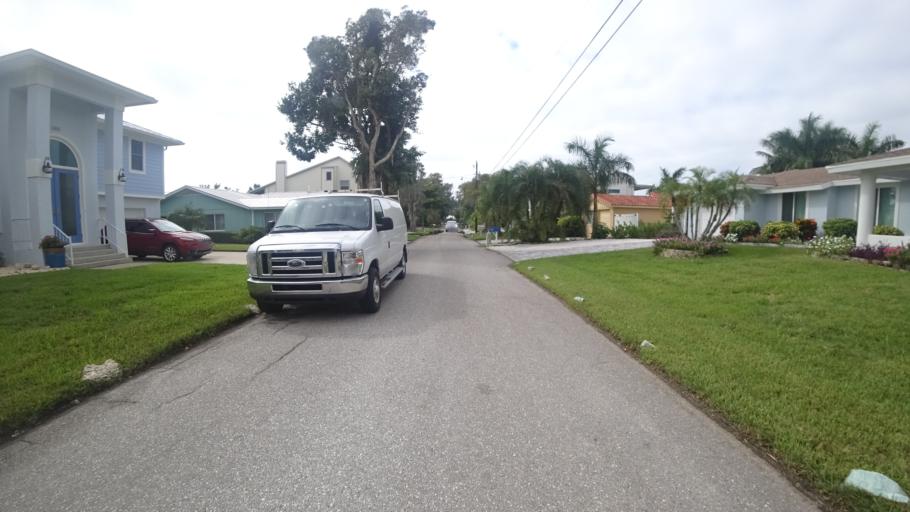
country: US
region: Florida
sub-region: Manatee County
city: Longboat Key
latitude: 27.4286
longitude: -82.6718
